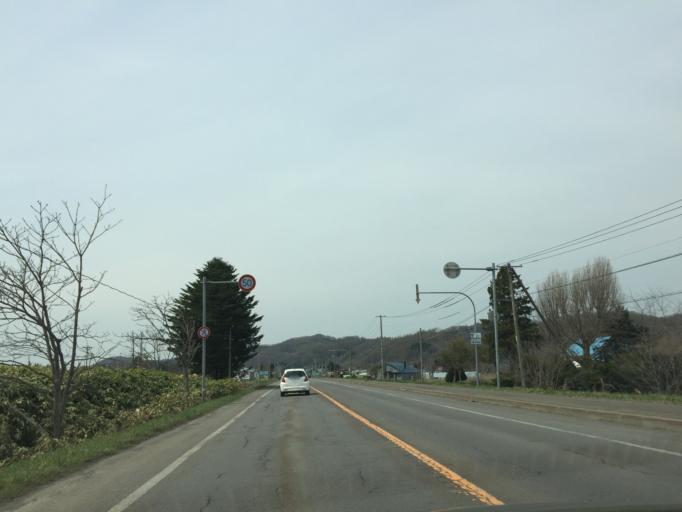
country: JP
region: Hokkaido
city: Ashibetsu
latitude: 43.5400
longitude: 142.1369
